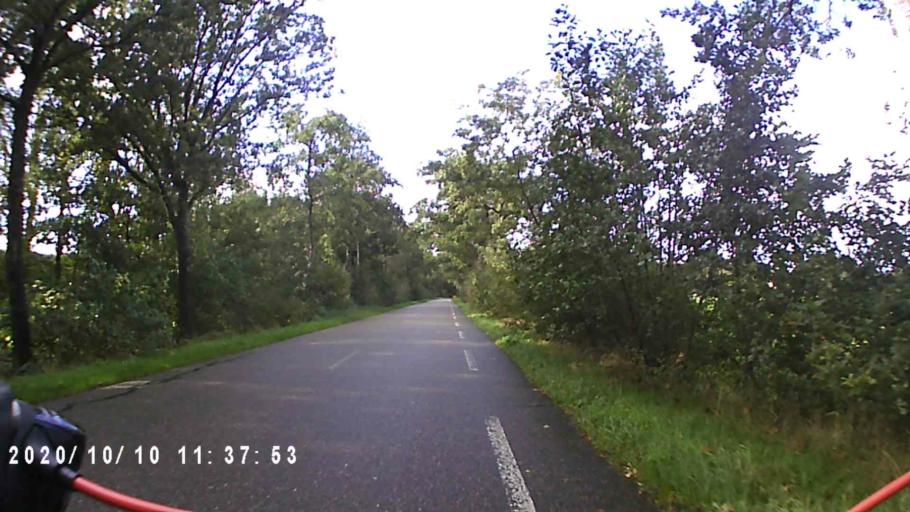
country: NL
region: Friesland
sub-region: Gemeente Smallingerland
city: Drachten
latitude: 53.0724
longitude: 6.1125
